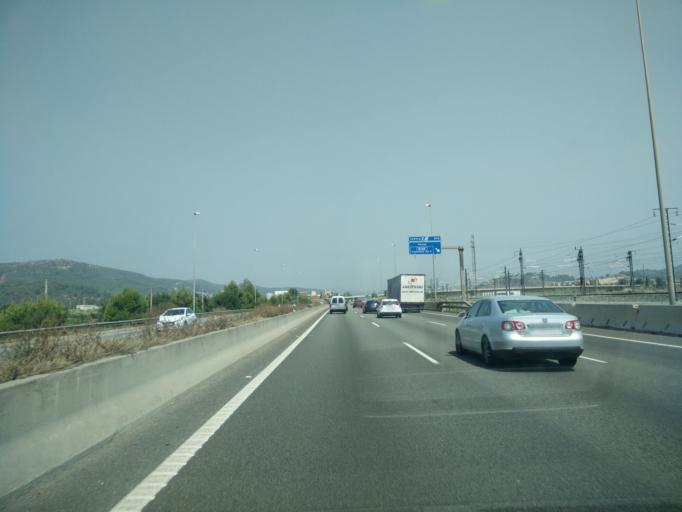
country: ES
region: Catalonia
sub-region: Provincia de Barcelona
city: Sant Vicenc dels Horts
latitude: 41.4027
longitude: 2.0129
